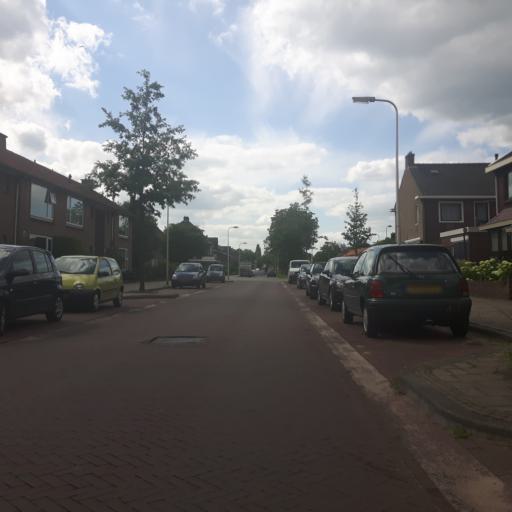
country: NL
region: Overijssel
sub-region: Gemeente Enschede
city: Enschede
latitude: 52.2137
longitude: 6.8665
